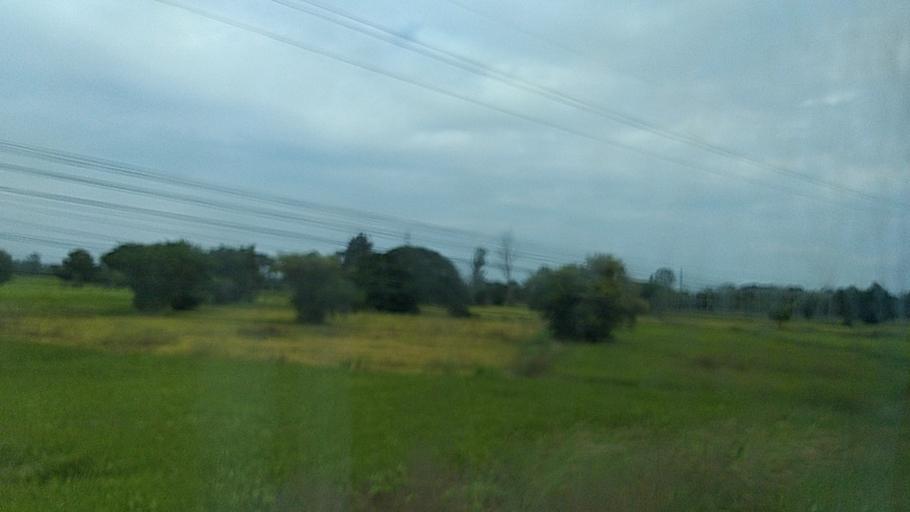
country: TH
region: Roi Et
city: Changhan
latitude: 16.1037
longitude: 103.5210
